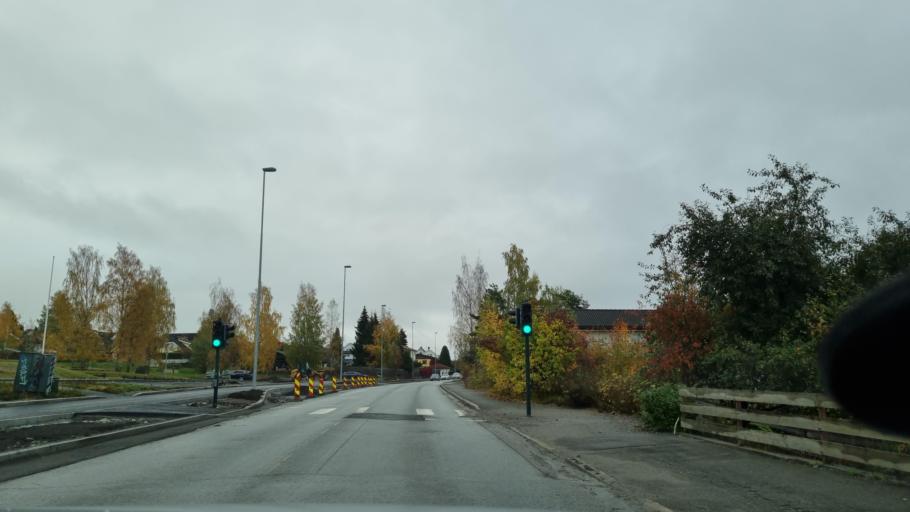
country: NO
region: Hedmark
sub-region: Hamar
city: Hamar
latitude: 60.8049
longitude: 11.0567
